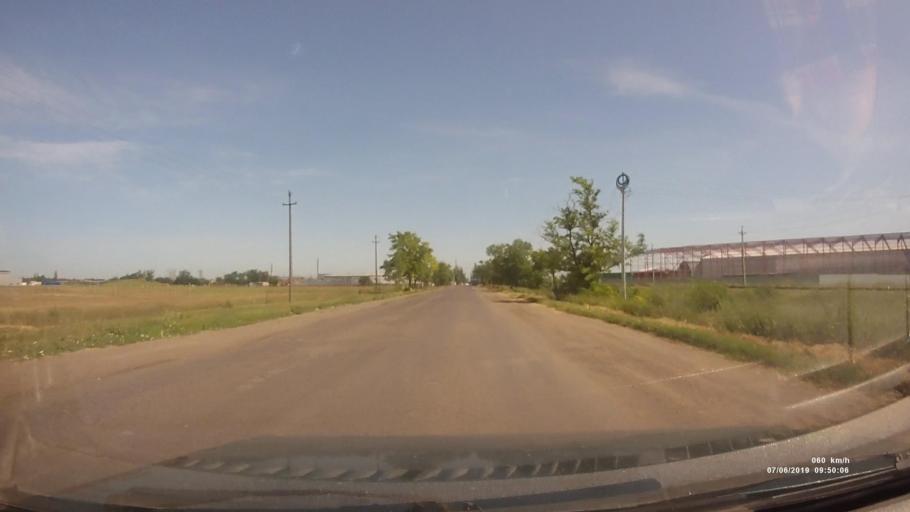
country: RU
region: Rostov
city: Azov
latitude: 47.0764
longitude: 39.4376
